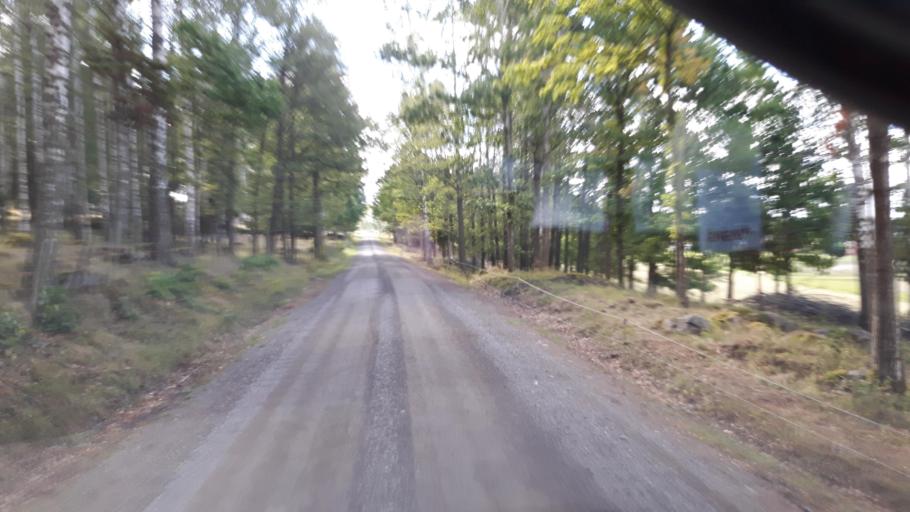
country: SE
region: OEstergoetland
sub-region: Kinda Kommun
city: Kisa
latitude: 58.0144
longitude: 15.6556
